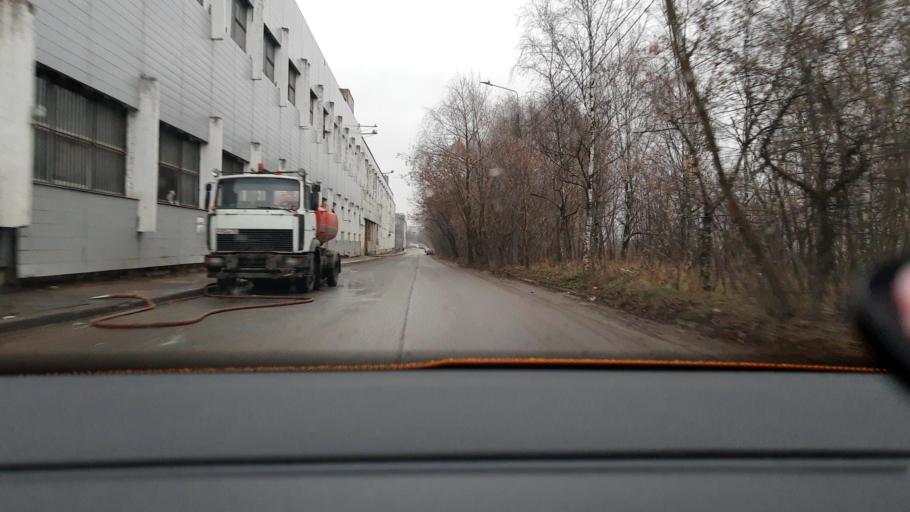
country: RU
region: Moscow
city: Strogino
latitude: 55.8299
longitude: 37.3990
